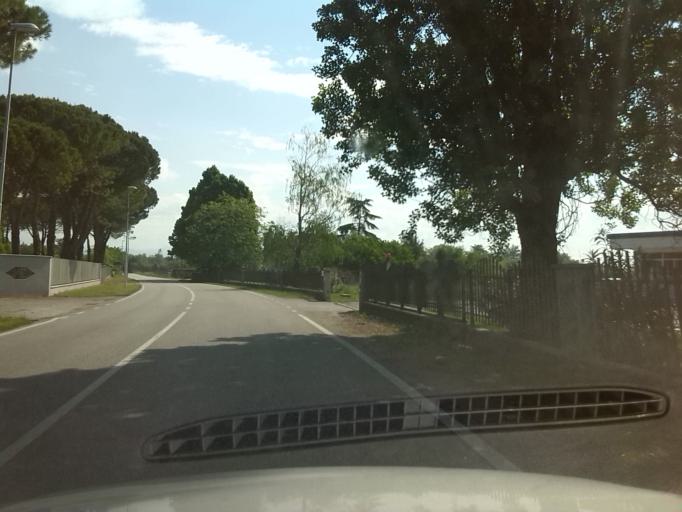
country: IT
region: Friuli Venezia Giulia
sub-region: Provincia di Udine
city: San Giovanni al Natisone
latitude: 45.9832
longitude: 13.4151
